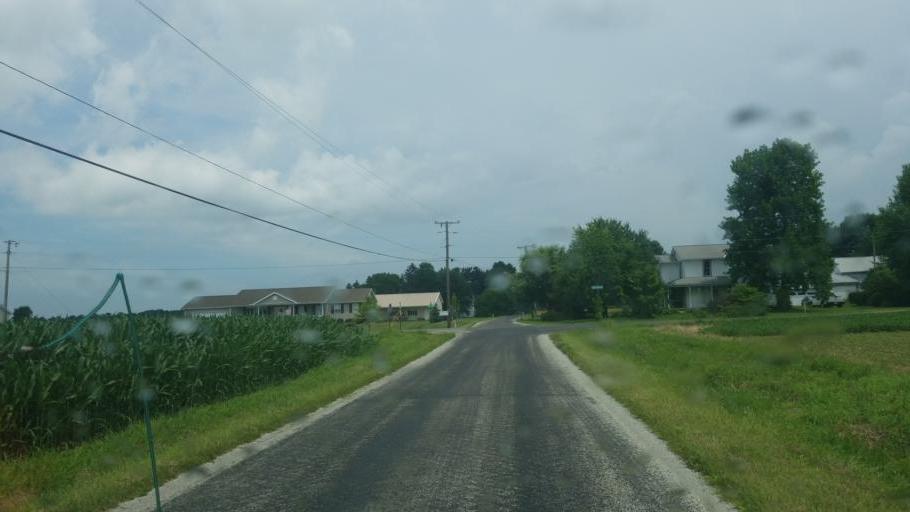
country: US
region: Ohio
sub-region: Wayne County
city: West Salem
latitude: 40.8576
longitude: -82.1255
